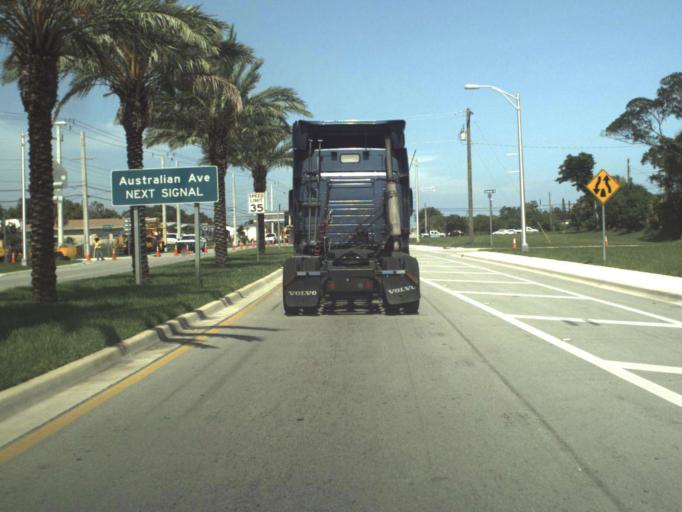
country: US
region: Florida
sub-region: Palm Beach County
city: Mangonia Park
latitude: 26.7695
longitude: -80.0736
